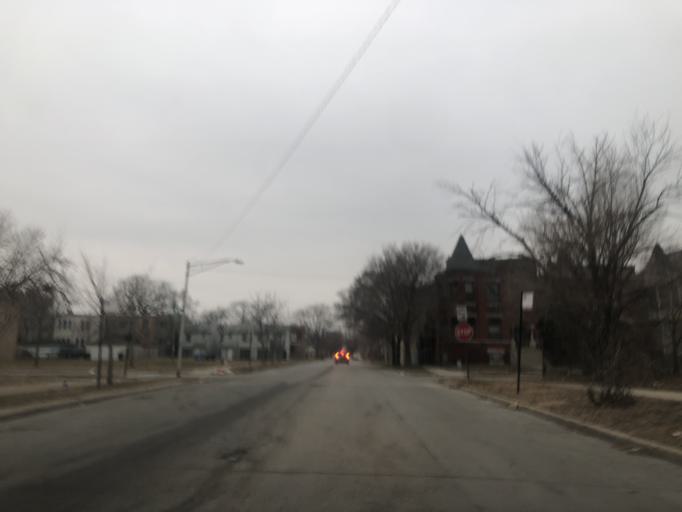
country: US
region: Illinois
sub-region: Cook County
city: Chicago
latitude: 41.7786
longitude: -87.6066
